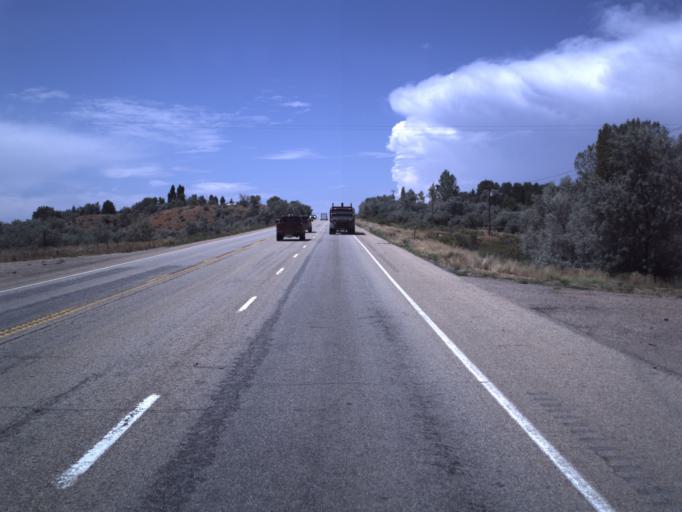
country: US
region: Utah
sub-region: Duchesne County
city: Roosevelt
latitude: 40.3019
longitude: -109.8855
